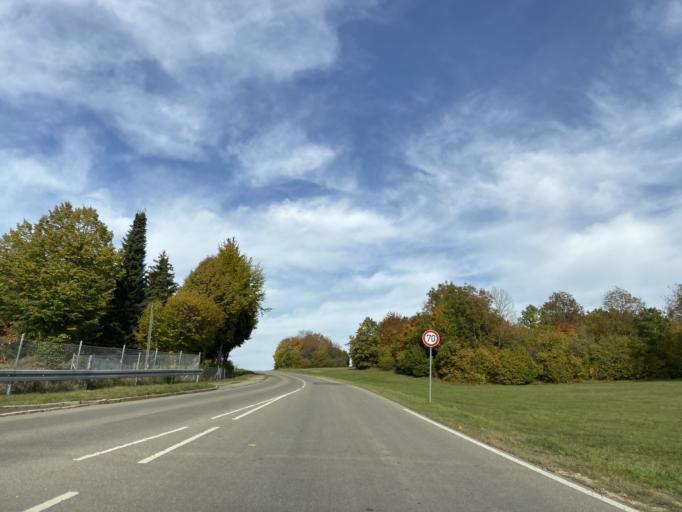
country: DE
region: Baden-Wuerttemberg
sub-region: Tuebingen Region
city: Schwenningen
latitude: 48.1014
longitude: 9.0087
